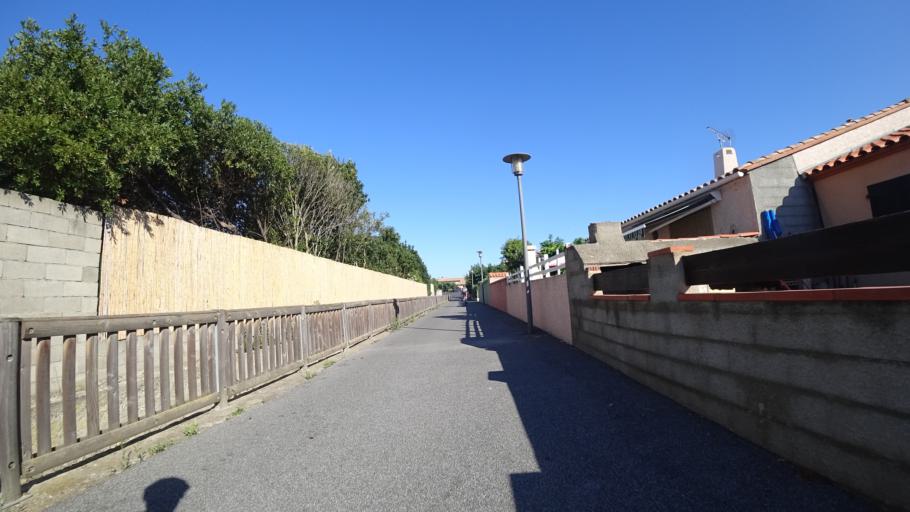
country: FR
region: Languedoc-Roussillon
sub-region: Departement des Pyrenees-Orientales
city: Sainte-Marie-Plage
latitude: 42.7284
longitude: 3.0182
